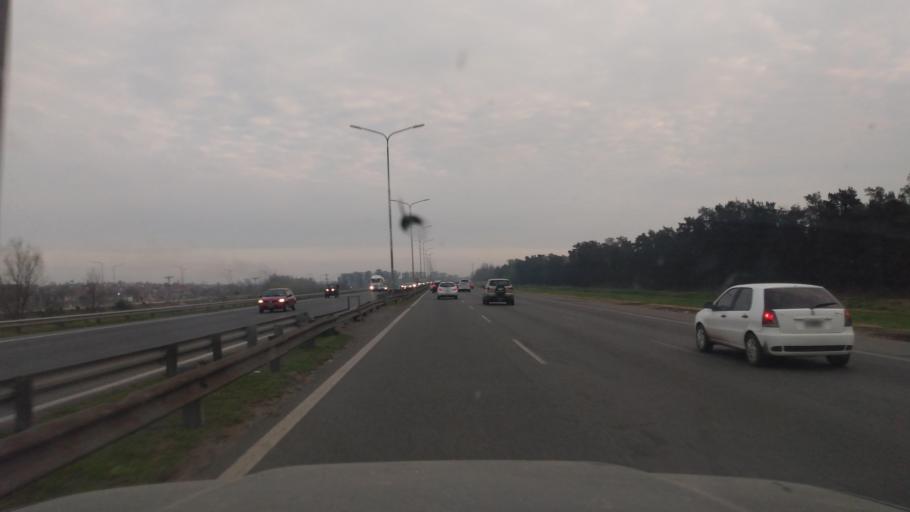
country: AR
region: Buenos Aires
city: Hurlingham
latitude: -34.5398
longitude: -58.6001
